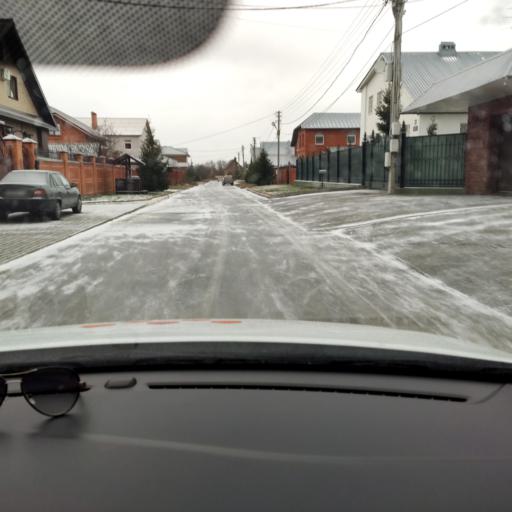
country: RU
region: Tatarstan
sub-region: Gorod Kazan'
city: Kazan
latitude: 55.8185
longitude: 49.2258
